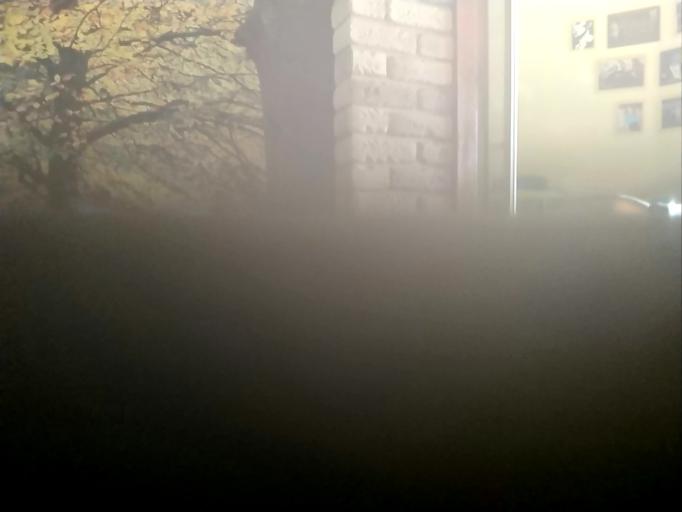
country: RU
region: Kaluga
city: Yukhnov
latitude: 54.6951
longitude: 35.0535
